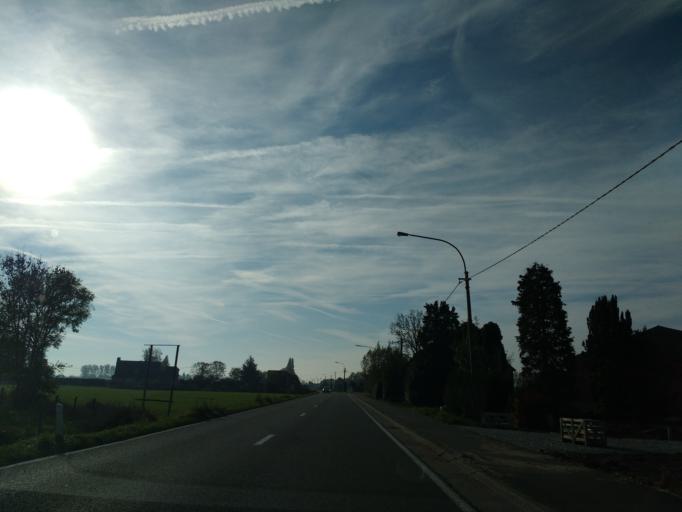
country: BE
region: Flanders
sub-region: Provincie Oost-Vlaanderen
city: Kaprijke
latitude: 51.2588
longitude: 3.6150
